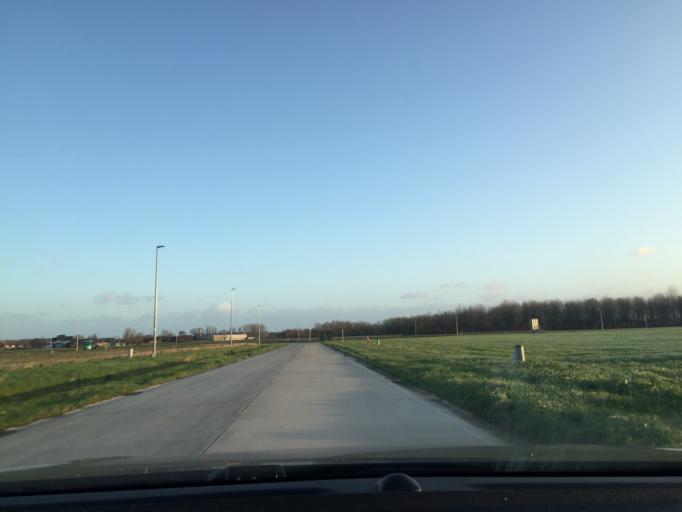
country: BE
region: Flanders
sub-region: Provincie West-Vlaanderen
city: Ardooie
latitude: 50.9757
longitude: 3.1586
